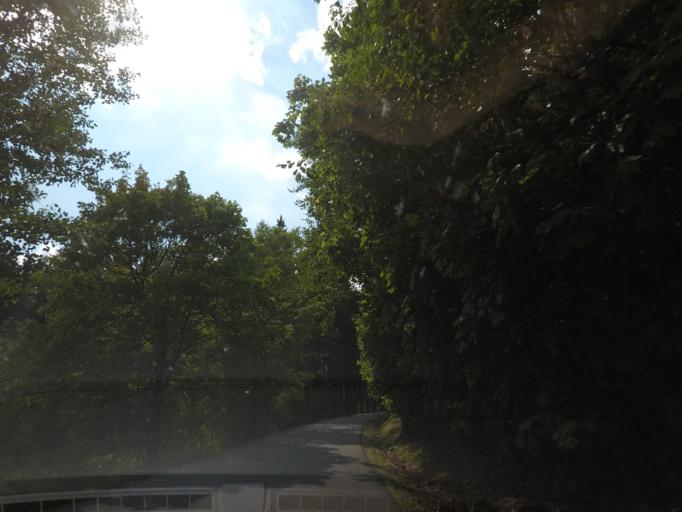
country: CZ
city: Radvanice
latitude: 50.6143
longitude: 16.0627
